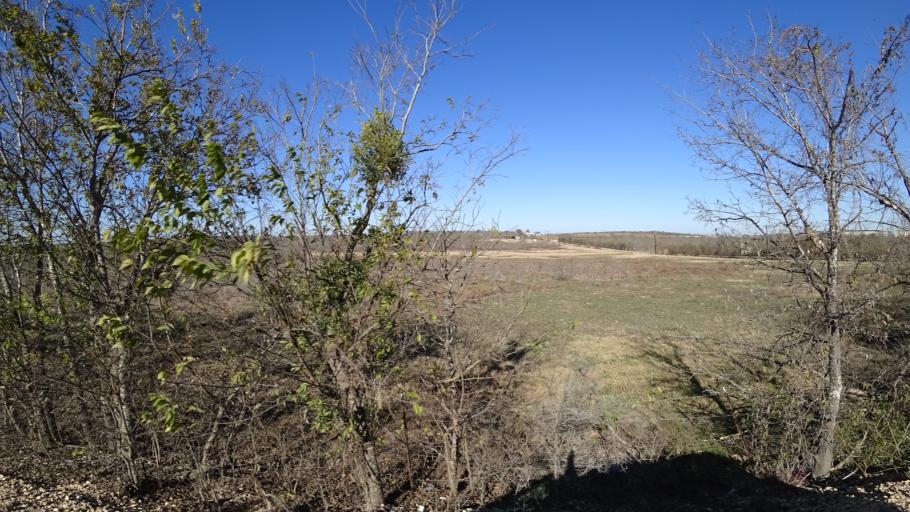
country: US
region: Texas
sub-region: Travis County
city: Onion Creek
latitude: 30.1105
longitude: -97.6704
